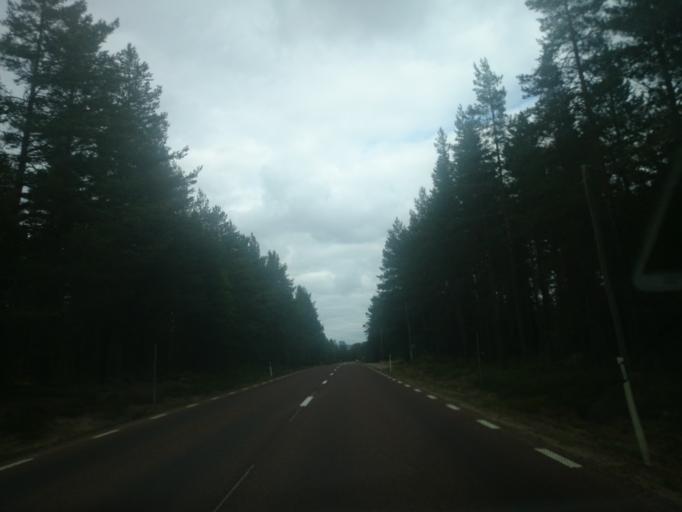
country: SE
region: Jaemtland
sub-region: Harjedalens Kommun
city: Sveg
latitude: 62.0575
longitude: 14.5674
